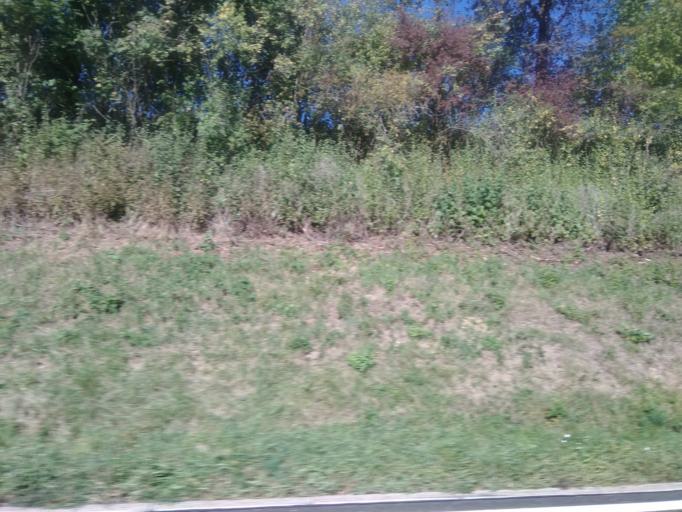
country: DE
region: Baden-Wuerttemberg
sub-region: Karlsruhe Region
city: Billigheim
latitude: 49.3536
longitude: 9.2756
